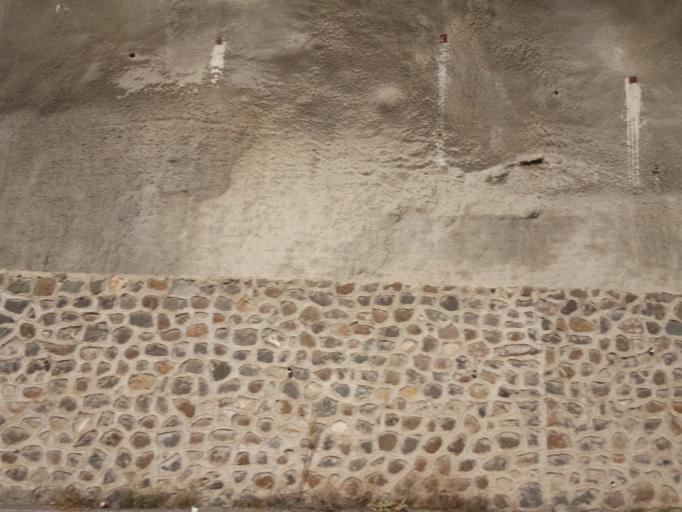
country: TR
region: Sivas
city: Koyulhisar
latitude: 40.2866
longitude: 37.7881
